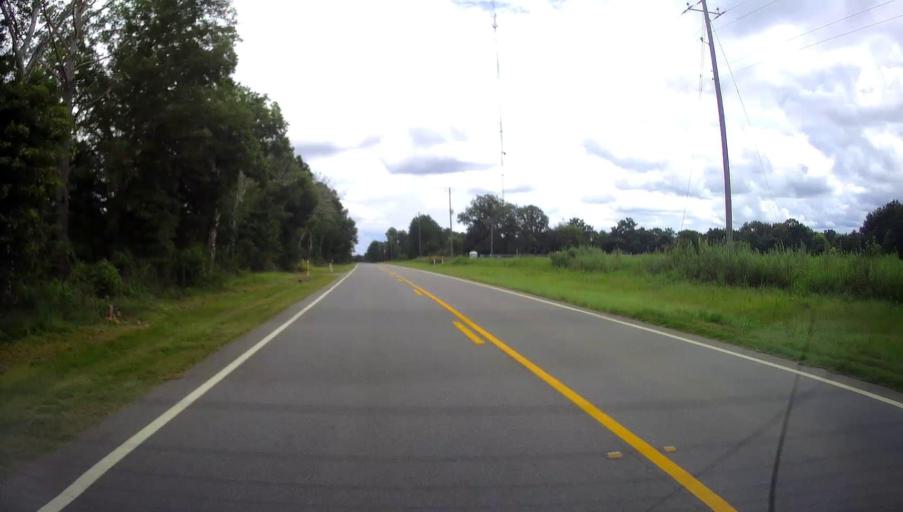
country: US
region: Georgia
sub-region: Macon County
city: Oglethorpe
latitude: 32.2675
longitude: -84.1093
